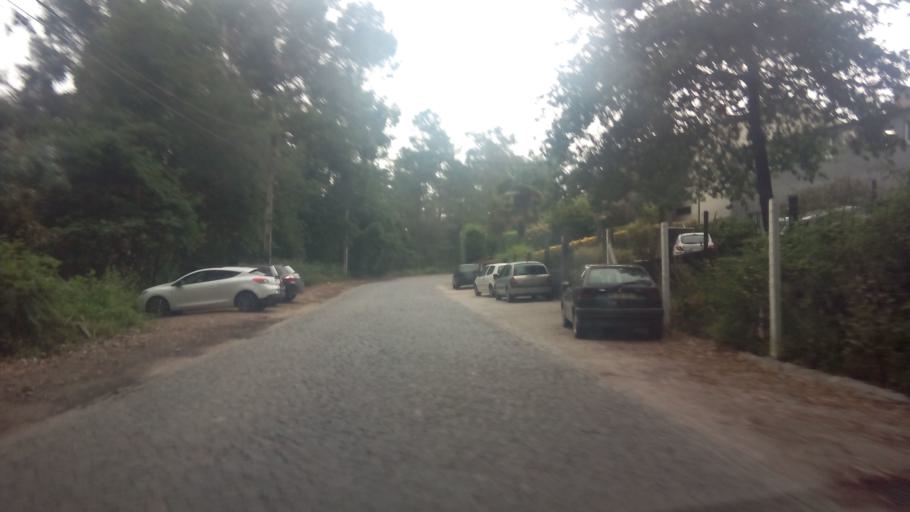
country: PT
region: Porto
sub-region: Paredes
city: Casteloes de Cepeda
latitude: 41.1882
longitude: -8.3450
